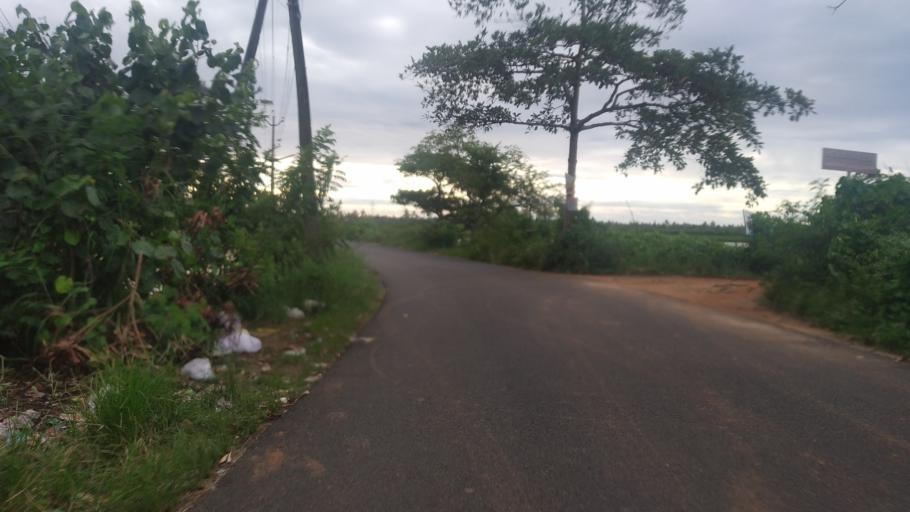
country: IN
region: Kerala
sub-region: Alappuzha
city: Arukutti
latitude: 9.8586
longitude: 76.2788
